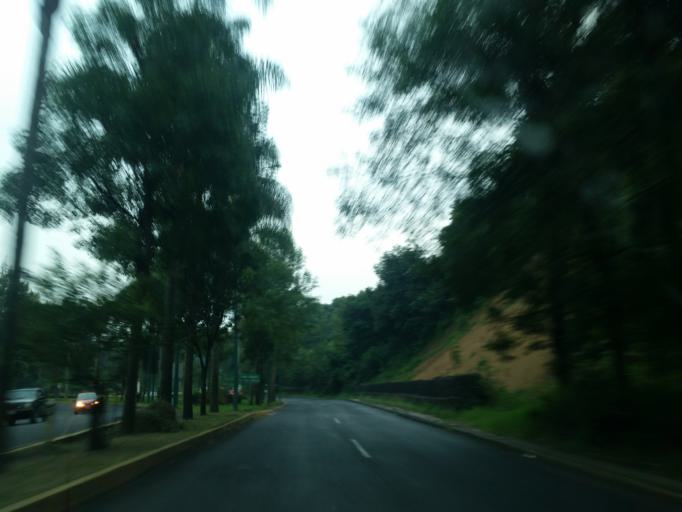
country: MX
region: Veracruz
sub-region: Xalapa
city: Xalapa de Enriquez
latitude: 19.5088
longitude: -96.9319
